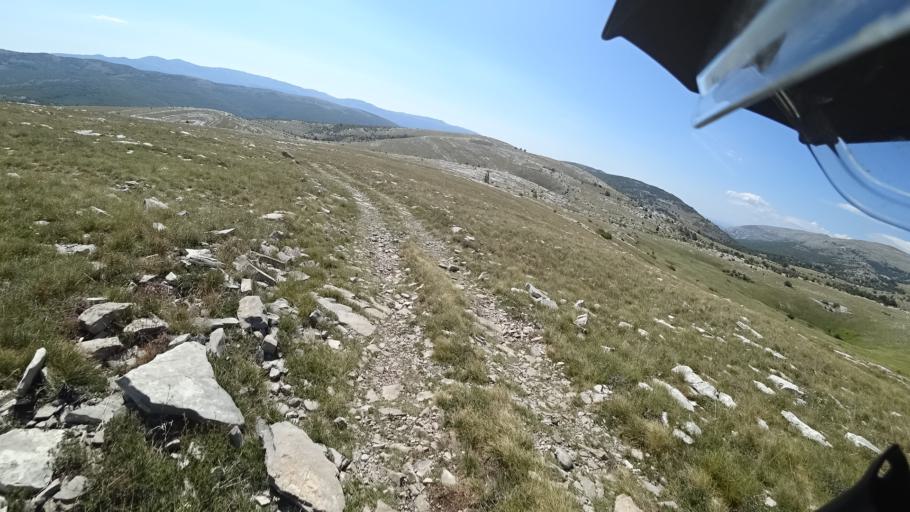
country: HR
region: Splitsko-Dalmatinska
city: Hrvace
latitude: 43.9014
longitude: 16.6003
